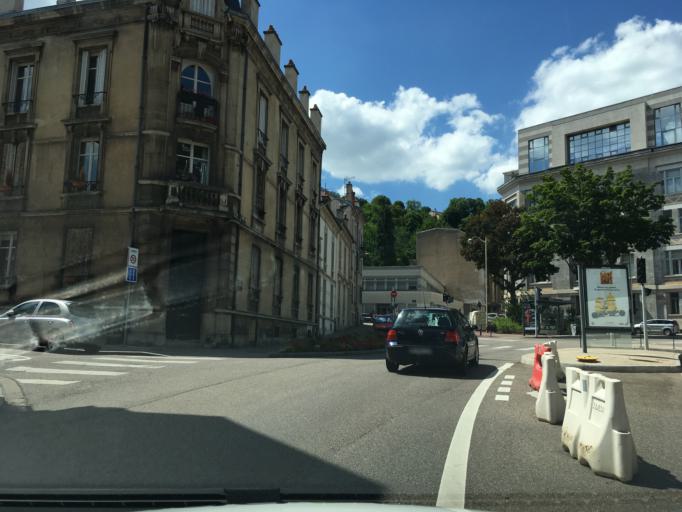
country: FR
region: Lorraine
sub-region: Departement de Meurthe-et-Moselle
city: Maxeville
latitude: 48.6929
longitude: 6.1658
